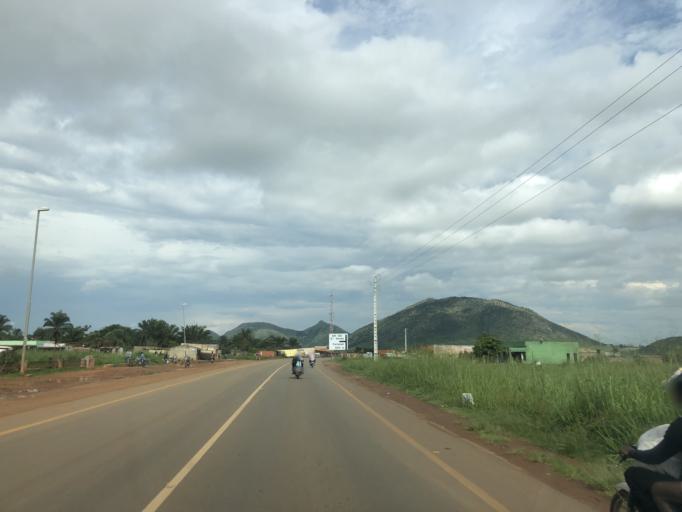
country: AO
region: Cuanza Sul
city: Uacu Cungo
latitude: -11.3501
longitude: 15.1075
